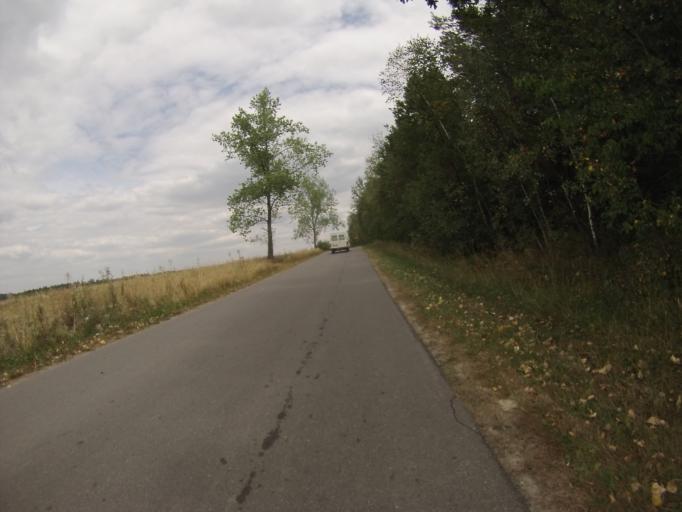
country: PL
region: Swietokrzyskie
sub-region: Powiat staszowski
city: Bogoria
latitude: 50.6826
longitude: 21.1943
